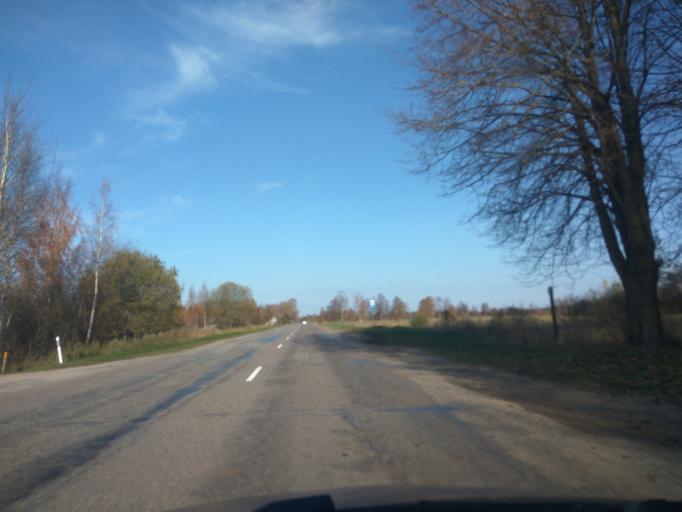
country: LV
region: Ventspils
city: Ventspils
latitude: 57.3169
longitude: 21.5584
